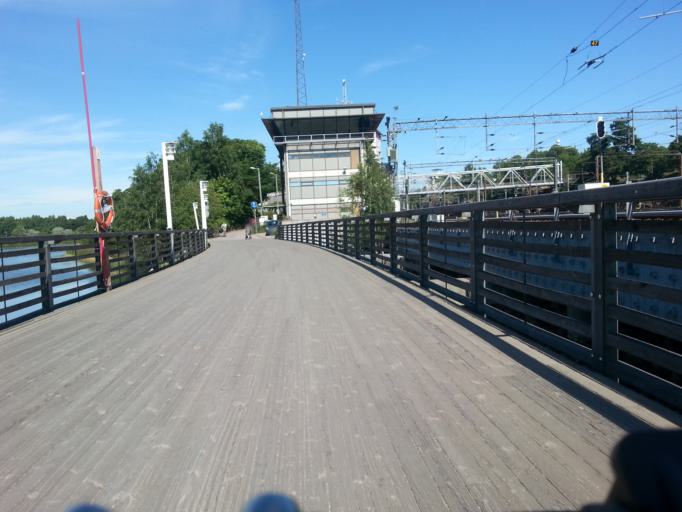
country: FI
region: Uusimaa
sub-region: Helsinki
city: Helsinki
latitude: 60.1799
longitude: 24.9383
